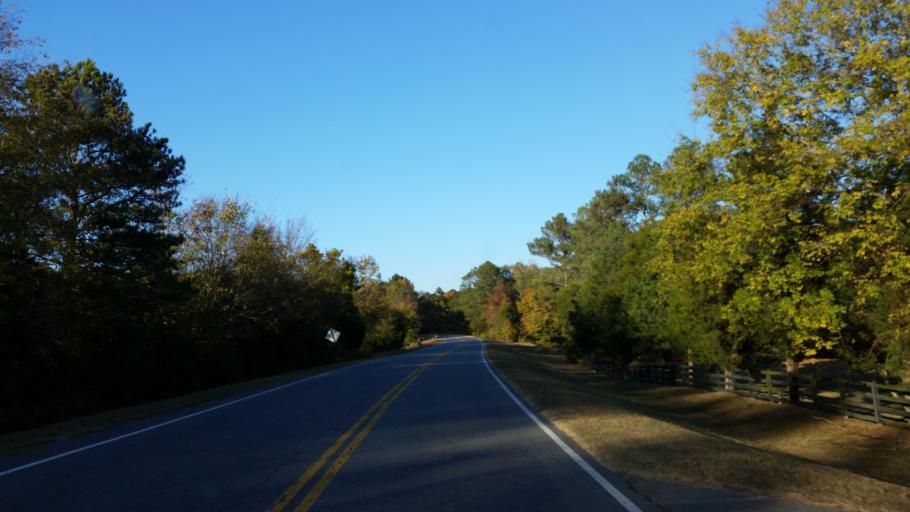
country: US
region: Georgia
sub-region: Bartow County
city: Adairsville
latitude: 34.3281
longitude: -84.9369
